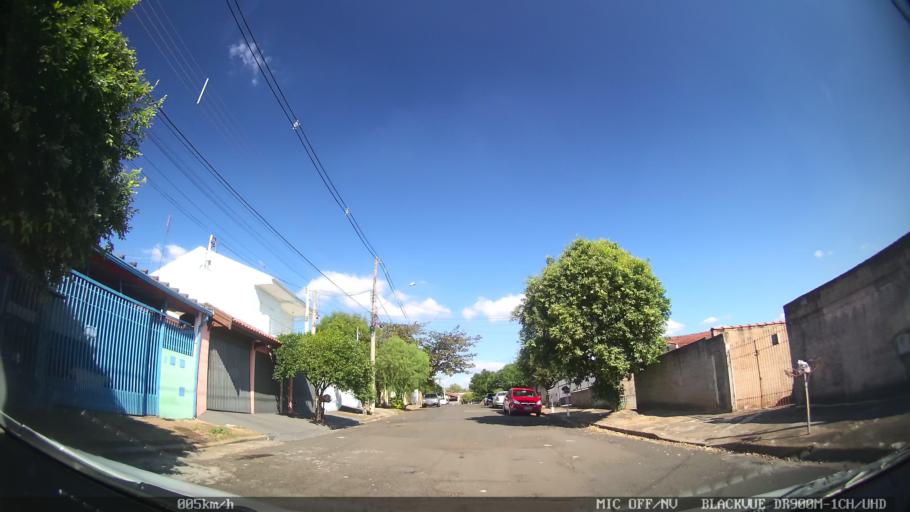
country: BR
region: Sao Paulo
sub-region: Sumare
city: Sumare
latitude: -22.8176
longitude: -47.2780
